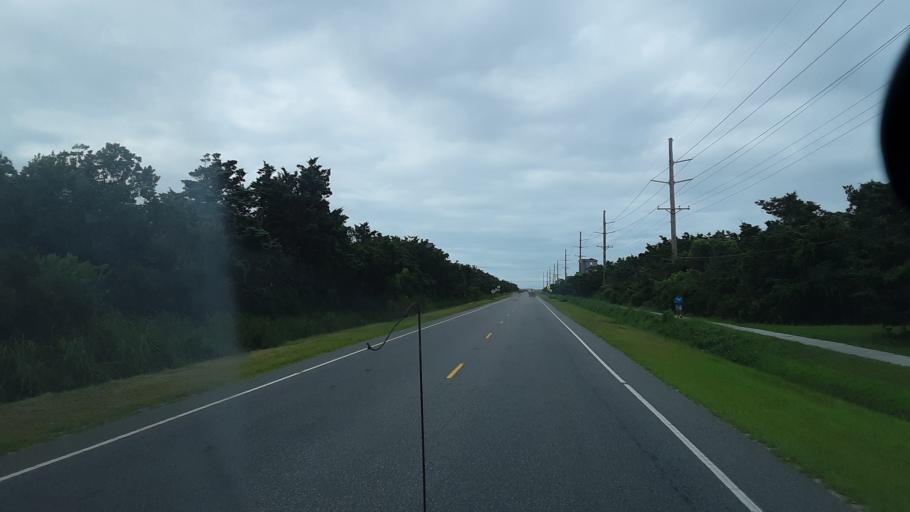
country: US
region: North Carolina
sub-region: Dare County
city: Buxton
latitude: 35.3286
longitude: -75.5080
